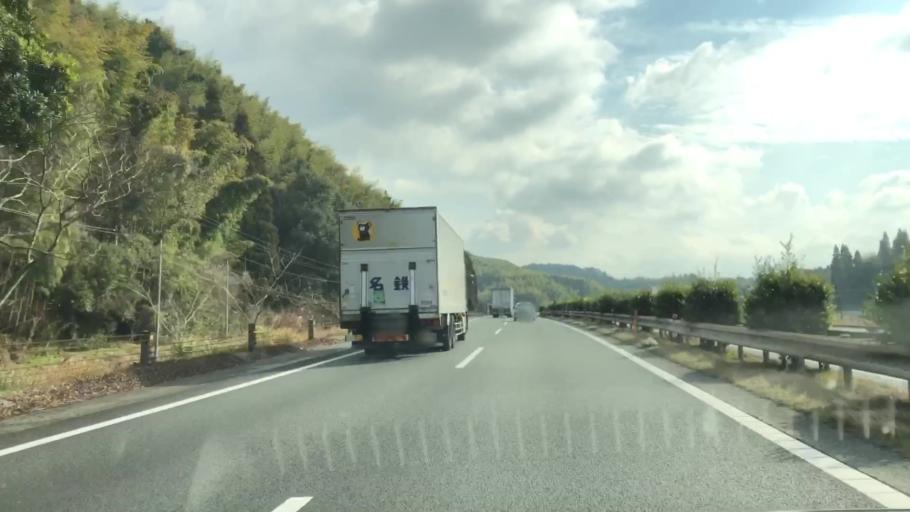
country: JP
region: Fukuoka
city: Setakamachi-takayanagi
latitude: 33.0880
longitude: 130.5400
